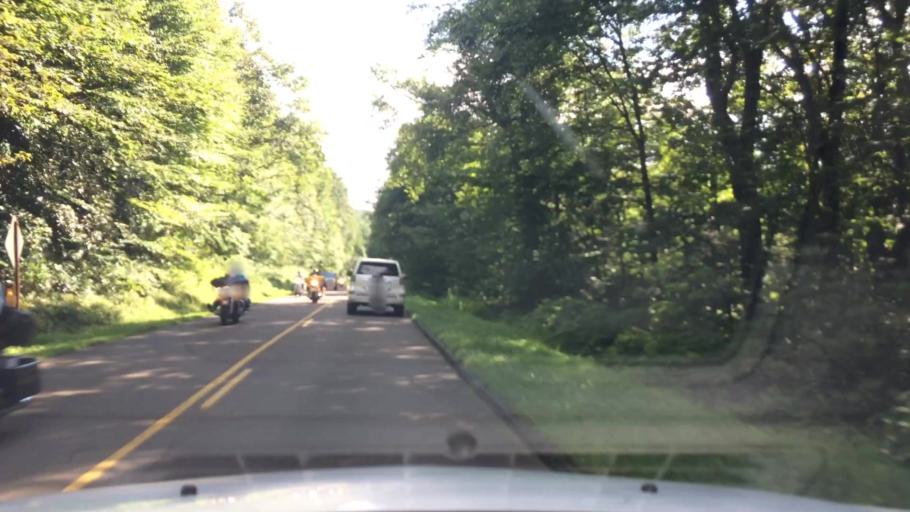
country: US
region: North Carolina
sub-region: Watauga County
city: Blowing Rock
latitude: 36.1479
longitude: -81.7045
